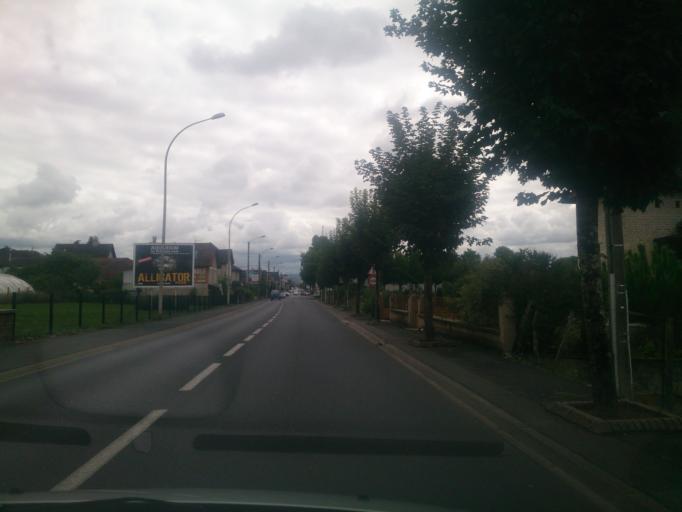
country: FR
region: Limousin
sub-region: Departement de la Correze
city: Ussac
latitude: 45.1647
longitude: 1.4998
